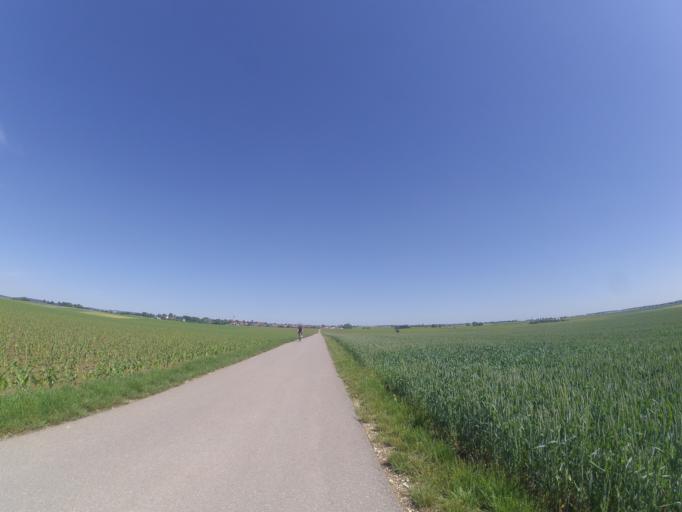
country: DE
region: Baden-Wuerttemberg
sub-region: Tuebingen Region
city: Dornstadt
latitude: 48.4696
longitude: 9.9166
